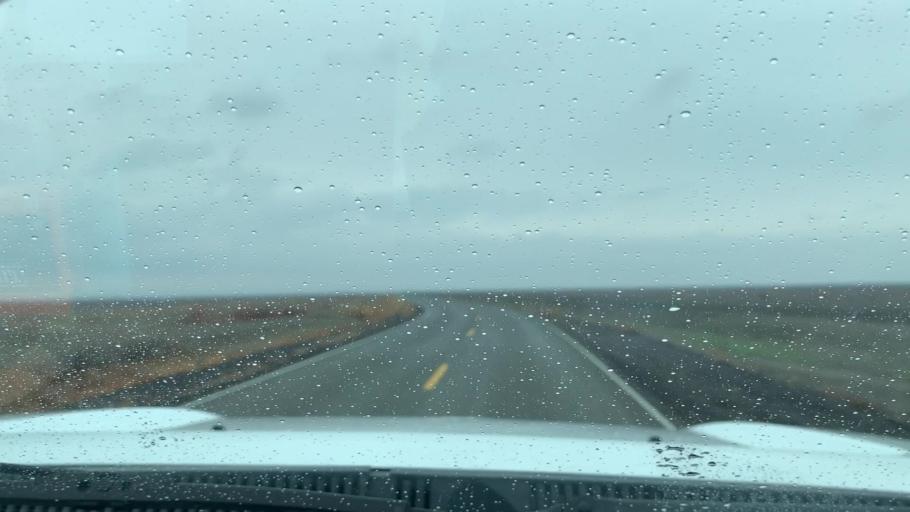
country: US
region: California
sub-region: Kings County
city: Corcoran
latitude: 35.9339
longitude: -119.7172
